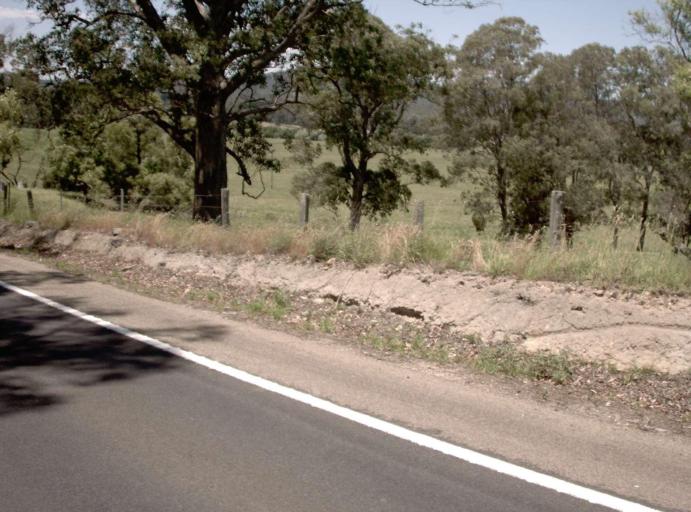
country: AU
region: Victoria
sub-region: East Gippsland
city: Lakes Entrance
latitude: -37.7061
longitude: 148.5516
